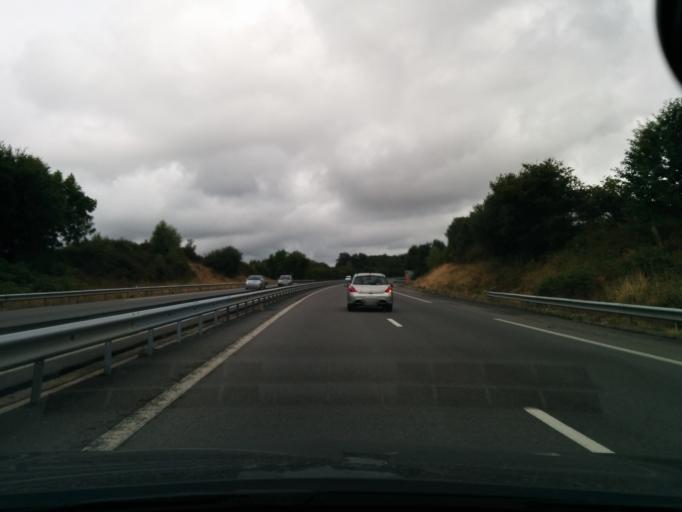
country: FR
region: Limousin
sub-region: Departement de la Correze
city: Uzerche
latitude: 45.5049
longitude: 1.5141
